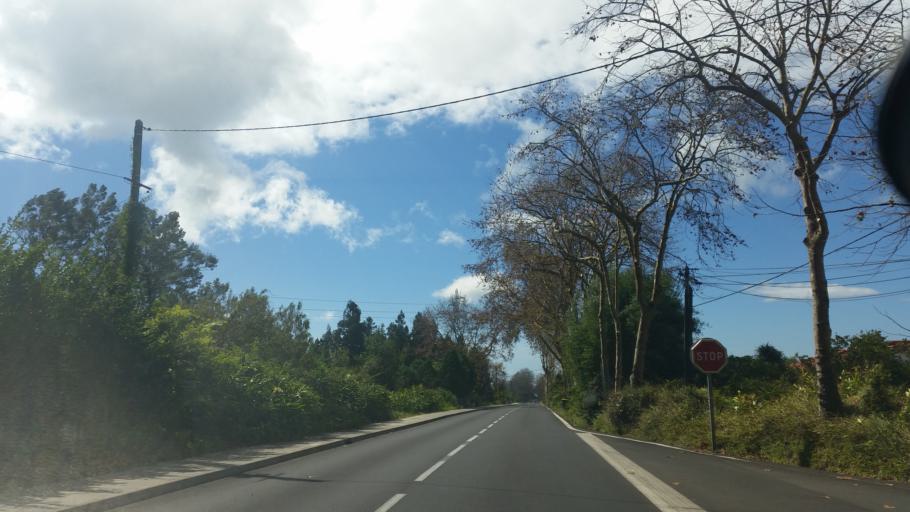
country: RE
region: Reunion
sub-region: Reunion
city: Saint-Benoit
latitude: -21.1238
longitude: 55.6401
